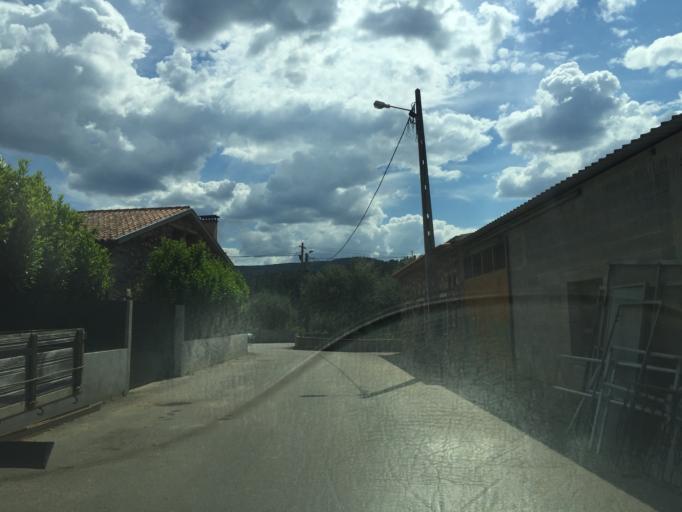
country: PT
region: Coimbra
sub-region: Pampilhosa da Serra
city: Pampilhosa da Serra
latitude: 40.0685
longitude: -7.8021
